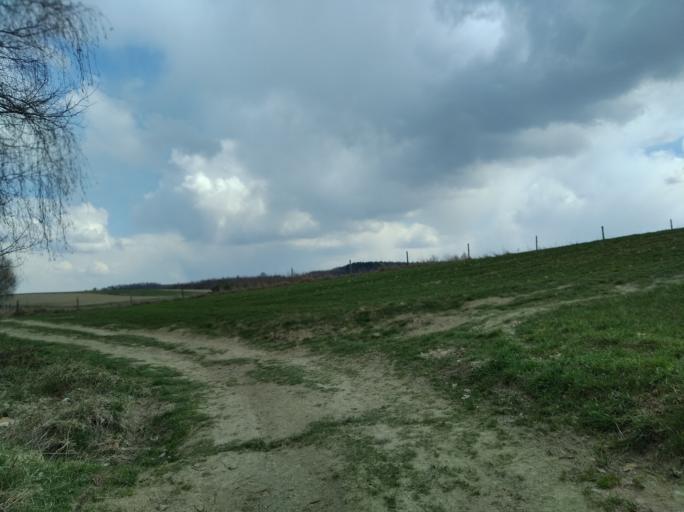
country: PL
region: Subcarpathian Voivodeship
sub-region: Powiat strzyzowski
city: Strzyzow
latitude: 49.9103
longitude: 21.7540
